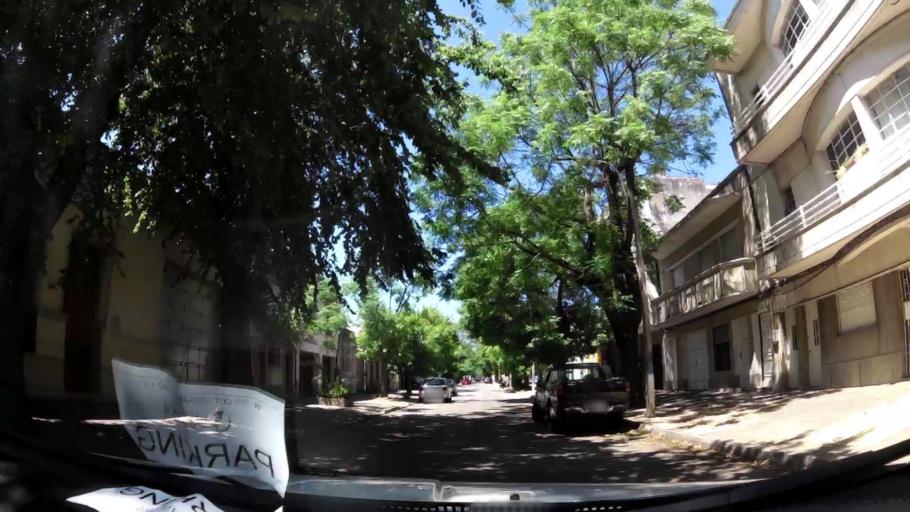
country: UY
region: Montevideo
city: Montevideo
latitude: -34.8858
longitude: -56.1711
